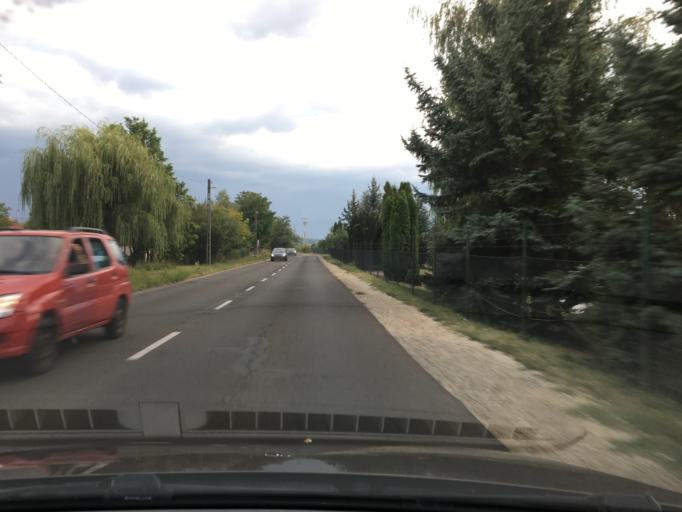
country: HU
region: Pest
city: Veresegyhaz
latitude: 47.6368
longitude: 19.3021
